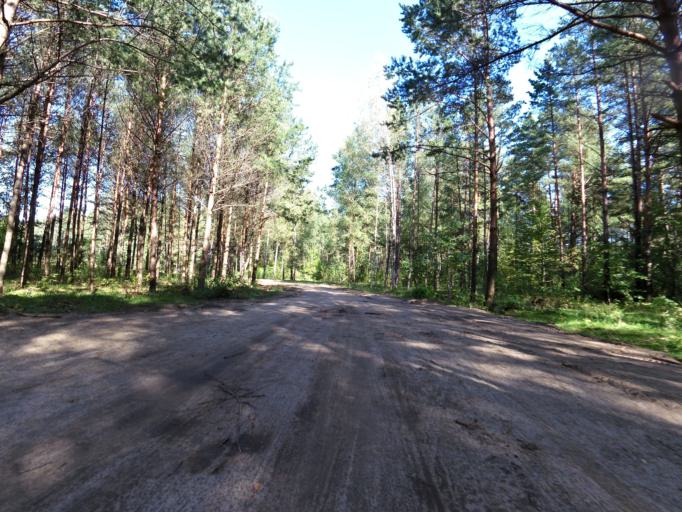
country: LT
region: Vilnius County
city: Lazdynai
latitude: 54.6785
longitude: 25.1925
